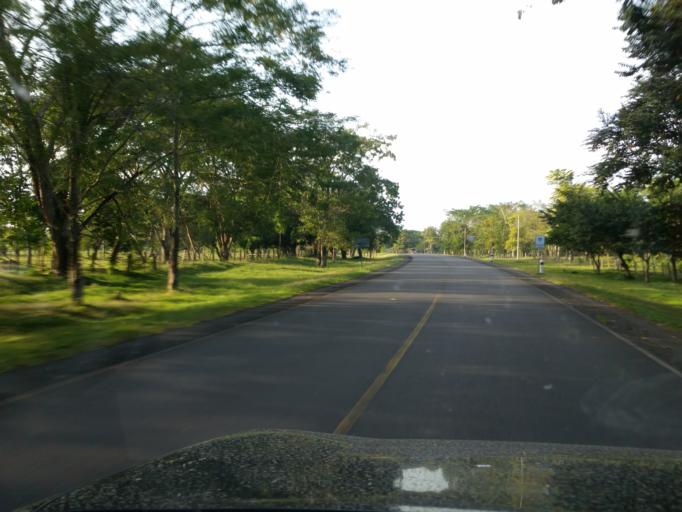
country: NI
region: Rio San Juan
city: San Miguelito
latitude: 11.3159
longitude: -84.7318
